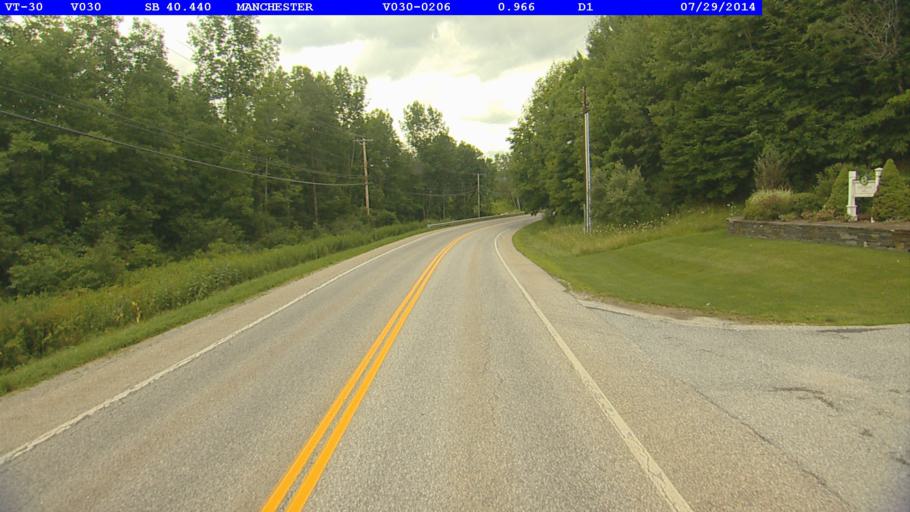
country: US
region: Vermont
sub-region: Bennington County
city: Manchester Center
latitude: 43.1904
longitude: -73.0559
